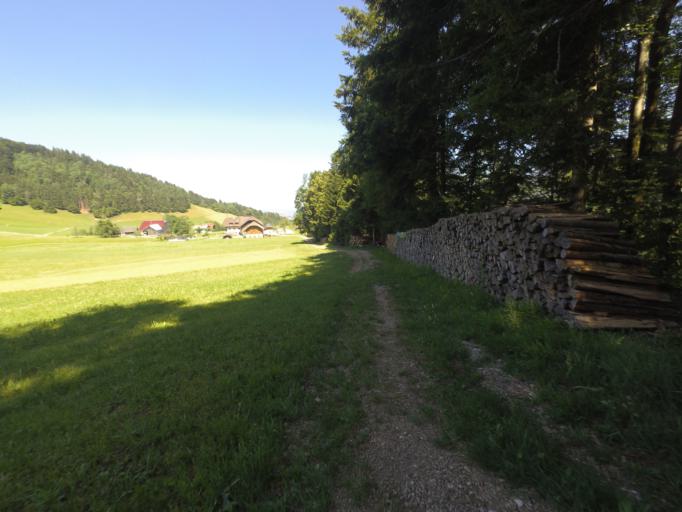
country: AT
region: Salzburg
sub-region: Politischer Bezirk Salzburg-Umgebung
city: Elsbethen
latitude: 47.7600
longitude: 13.1097
